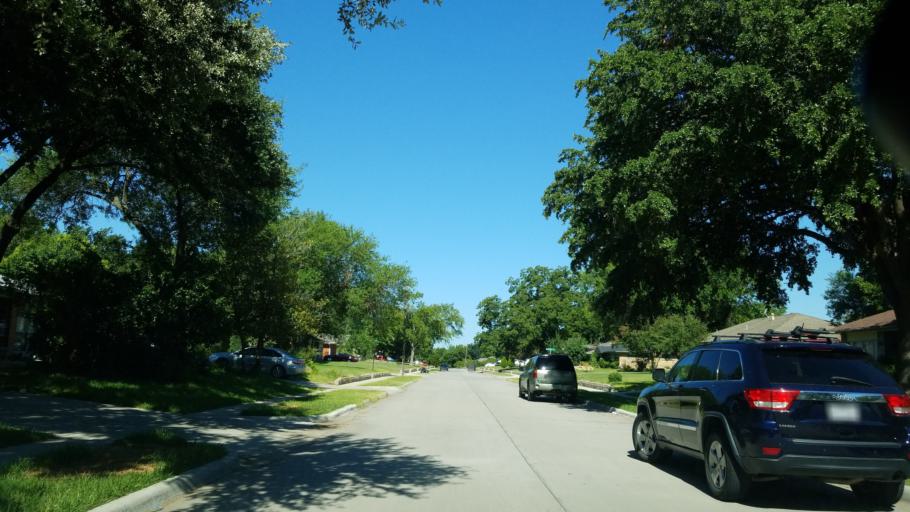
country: US
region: Texas
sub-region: Dallas County
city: Carrollton
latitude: 32.9598
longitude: -96.8921
